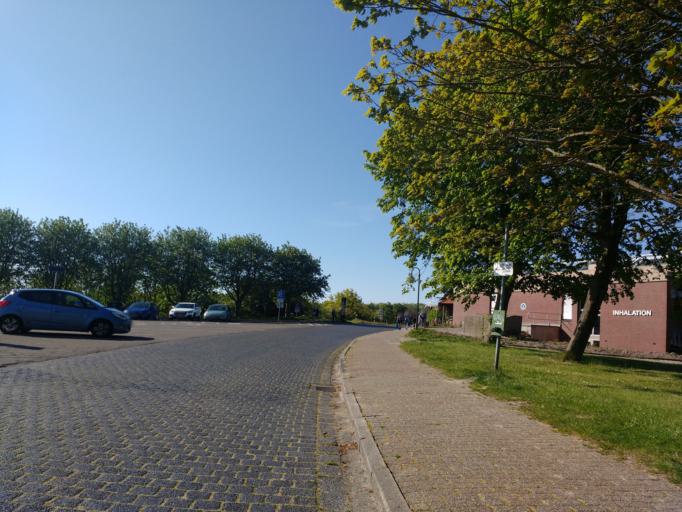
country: DE
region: Lower Saxony
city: Schillig
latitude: 53.6847
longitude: 8.0177
